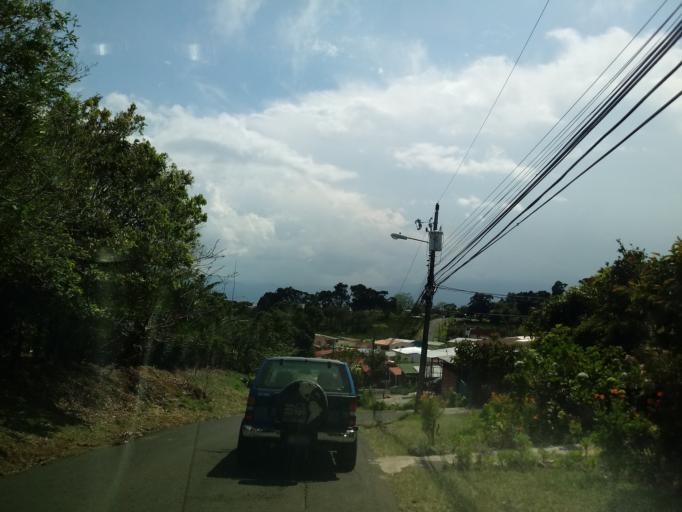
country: CR
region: Heredia
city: Angeles
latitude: 10.0312
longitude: -84.0378
